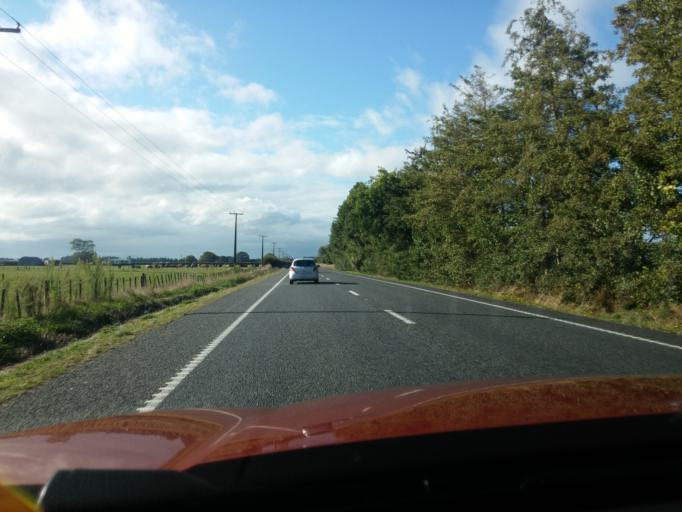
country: NZ
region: Waikato
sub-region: Hauraki District
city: Paeroa
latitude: -37.5655
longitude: 175.5508
